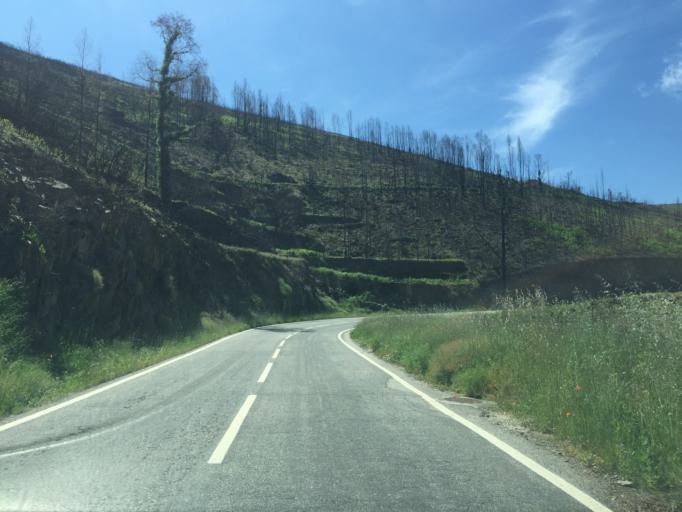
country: PT
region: Coimbra
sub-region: Pampilhosa da Serra
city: Pampilhosa da Serra
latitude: 40.0335
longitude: -7.9598
